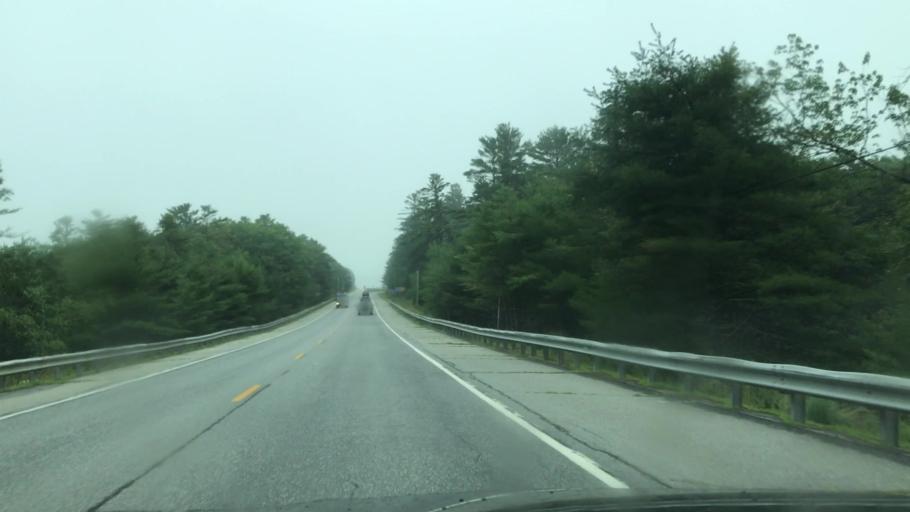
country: US
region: Maine
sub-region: Lincoln County
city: Damariscotta
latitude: 44.0495
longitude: -69.5052
